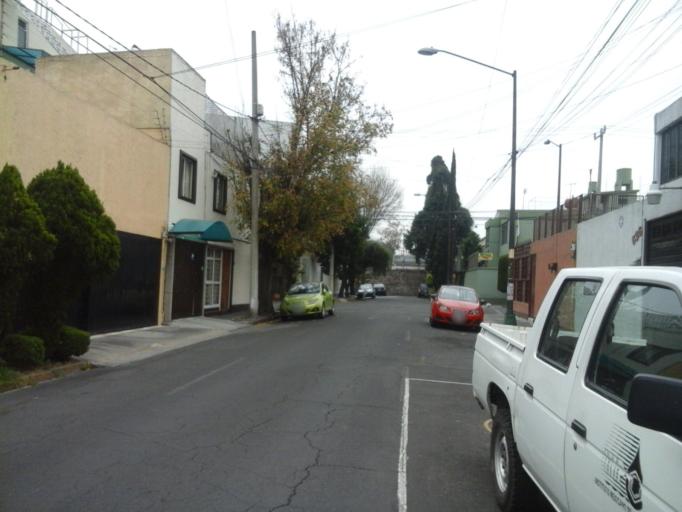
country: MX
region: Mexico
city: Colonia Lindavista
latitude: 19.4878
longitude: -99.1313
